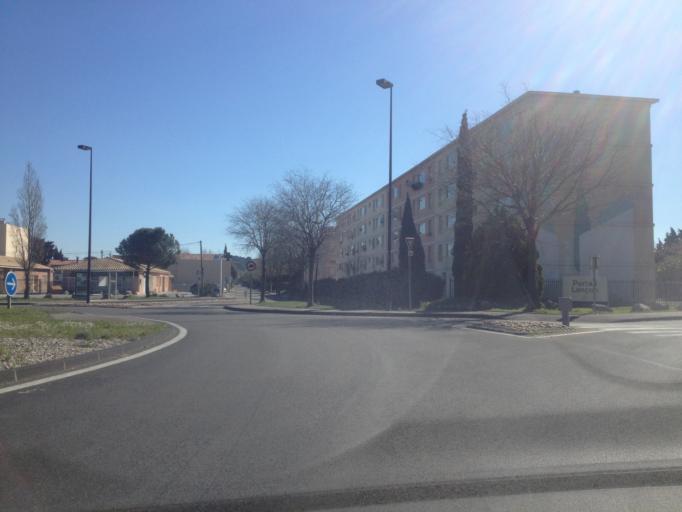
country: FR
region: Provence-Alpes-Cote d'Azur
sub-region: Departement du Vaucluse
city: Orange
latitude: 44.1475
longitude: 4.8088
